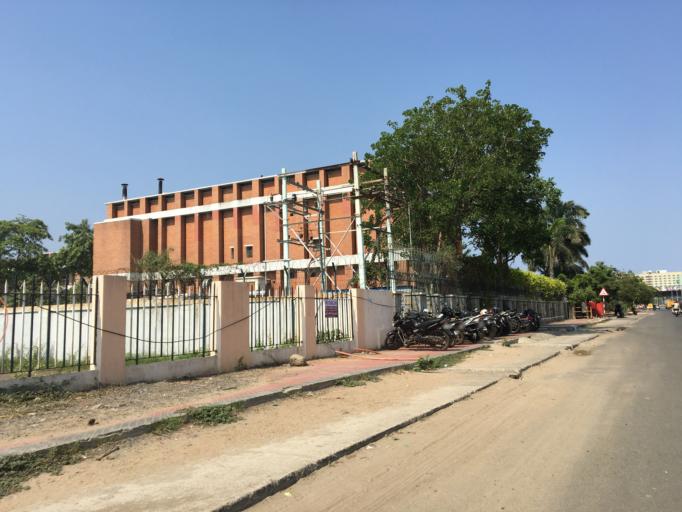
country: IN
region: Tamil Nadu
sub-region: Kancheepuram
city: Perungudi
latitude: 12.9812
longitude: 80.2451
